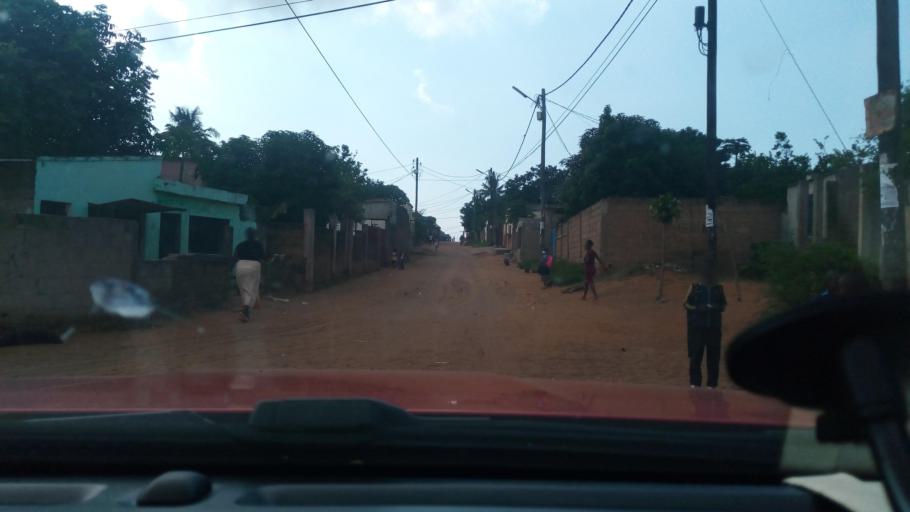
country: MZ
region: Maputo City
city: Maputo
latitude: -25.9206
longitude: 32.5979
